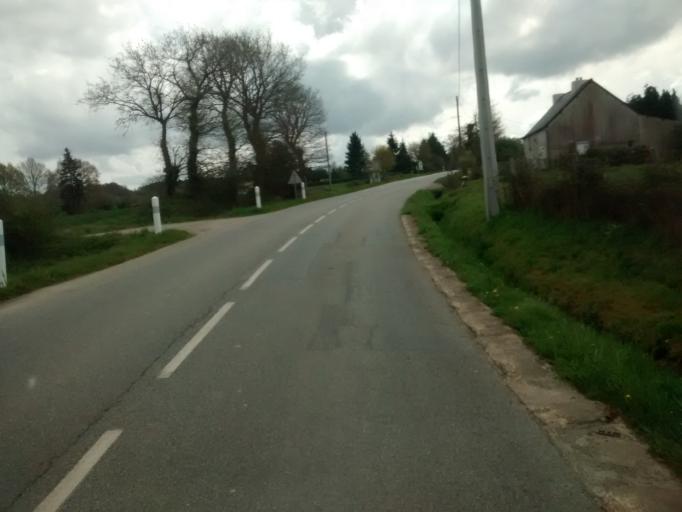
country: FR
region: Brittany
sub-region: Departement du Morbihan
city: Caro
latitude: 47.8876
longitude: -2.3606
